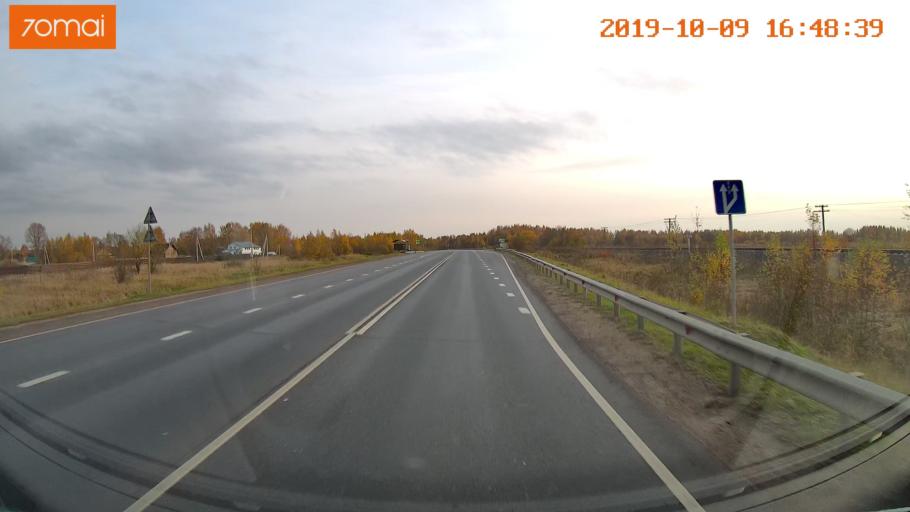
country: RU
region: Kostroma
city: Volgorechensk
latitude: 57.4258
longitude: 41.1906
